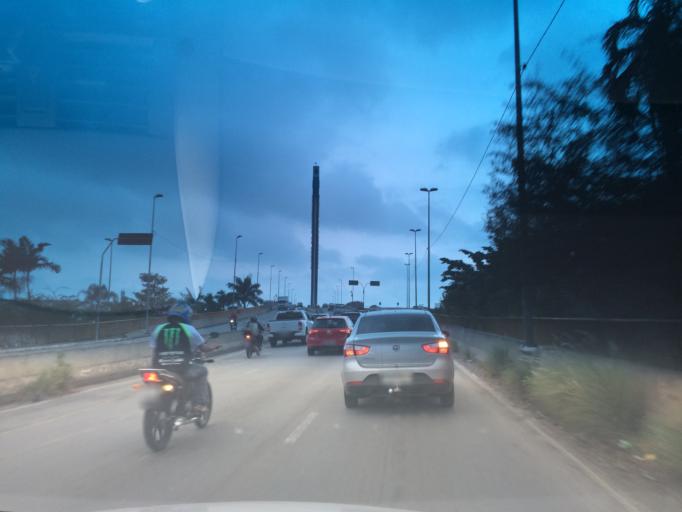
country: BR
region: Sao Paulo
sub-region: Guarulhos
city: Guarulhos
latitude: -23.4701
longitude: -46.5198
